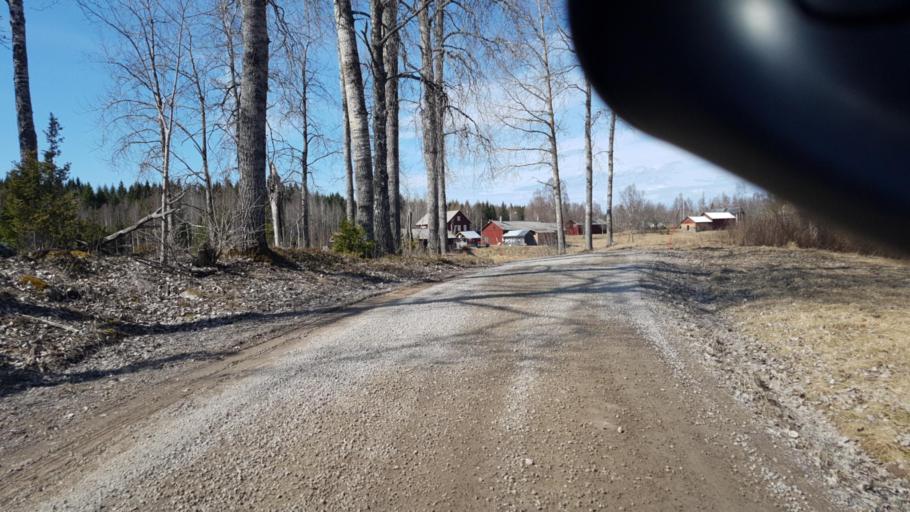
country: SE
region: Vaermland
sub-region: Arvika Kommun
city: Arvika
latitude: 59.5465
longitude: 12.8515
